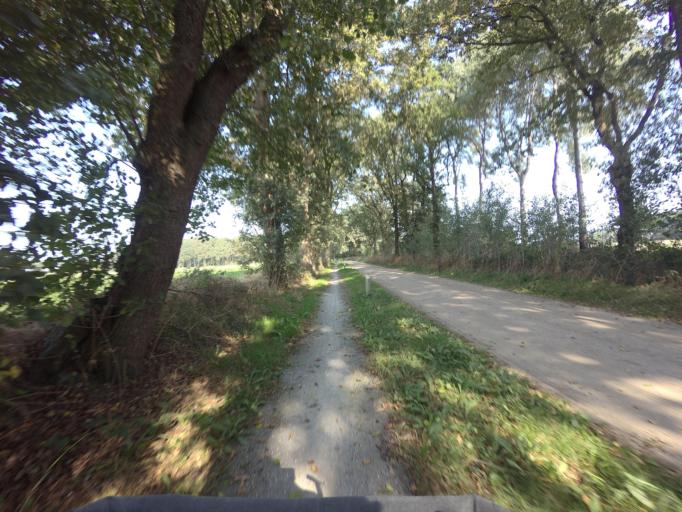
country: NL
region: Drenthe
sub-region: Gemeente Tynaarlo
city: Vries
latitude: 53.1057
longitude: 6.5329
